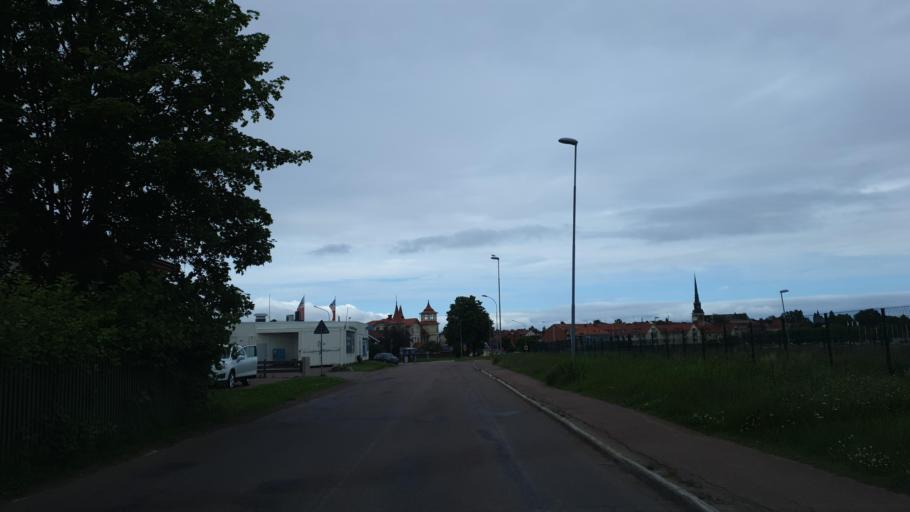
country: SE
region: Dalarna
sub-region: Mora Kommun
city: Mora
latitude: 61.0003
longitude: 14.5408
